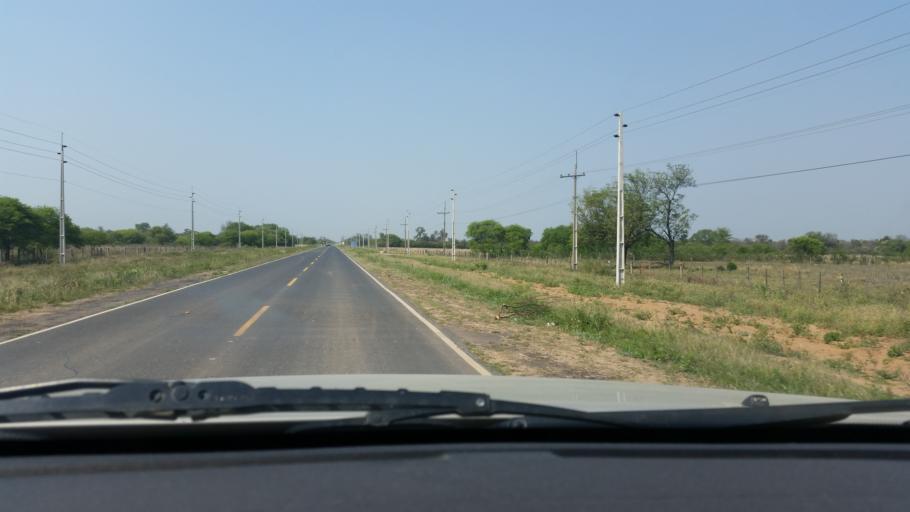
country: PY
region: Boqueron
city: Filadelfia
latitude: -22.4060
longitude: -60.0350
